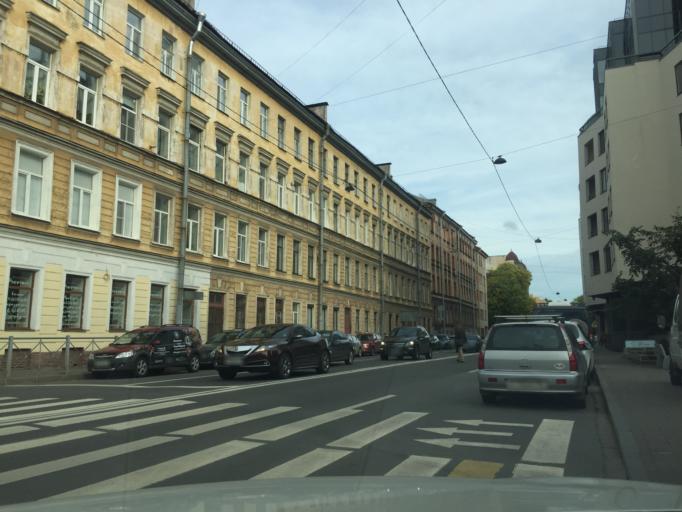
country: RU
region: St.-Petersburg
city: Centralniy
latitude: 59.9376
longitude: 30.3779
